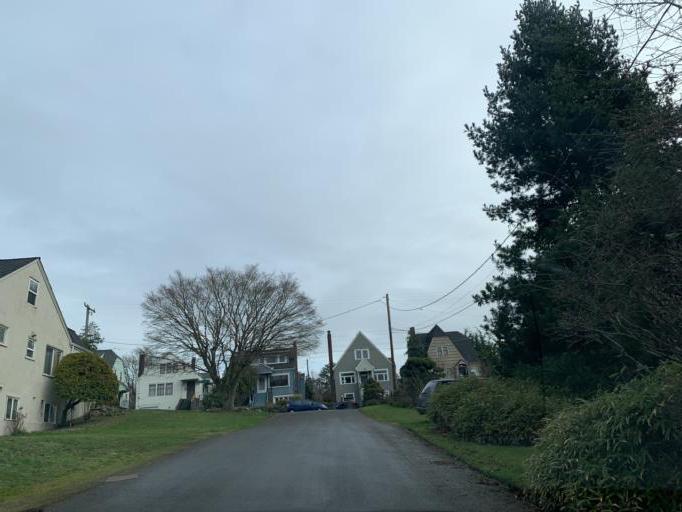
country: US
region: Washington
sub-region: King County
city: Seattle
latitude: 47.5743
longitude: -122.3155
